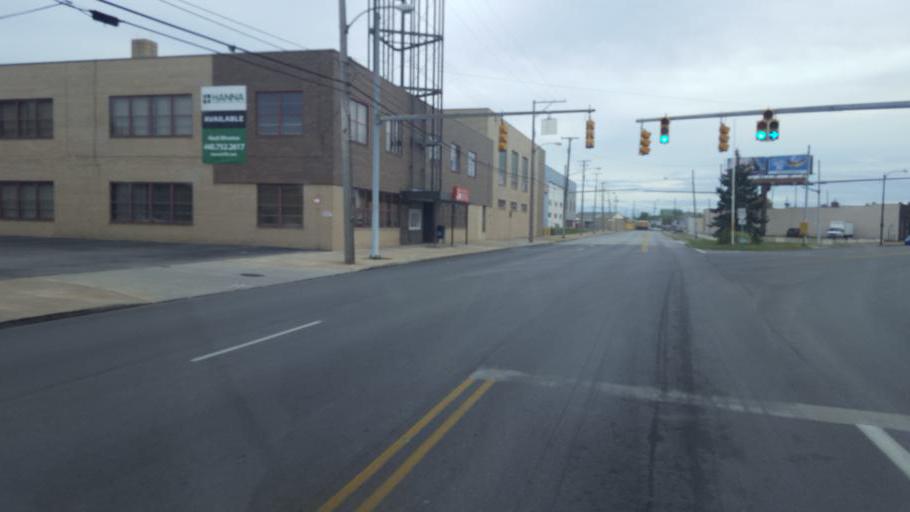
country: US
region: Ohio
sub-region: Lorain County
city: Lorain
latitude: 41.4565
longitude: -82.1671
